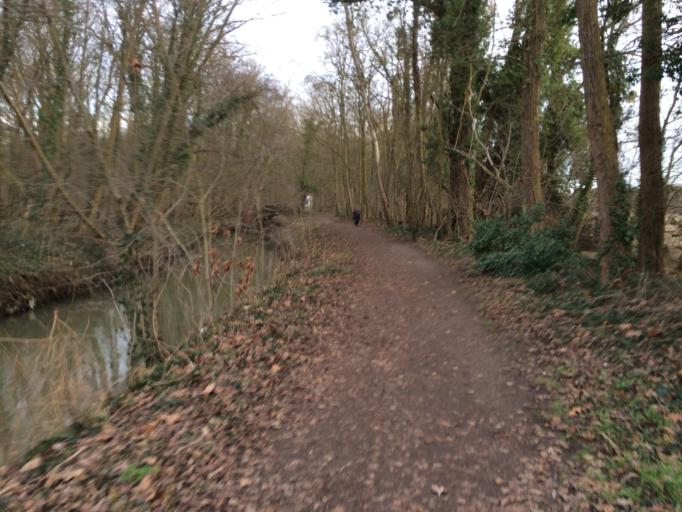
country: FR
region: Ile-de-France
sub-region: Departement de l'Essonne
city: Epinay-sur-Orge
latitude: 48.6839
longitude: 2.3215
